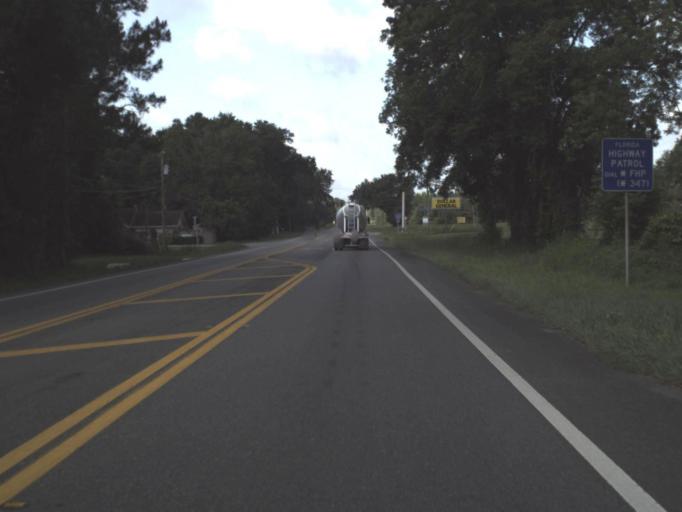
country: US
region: Florida
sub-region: Columbia County
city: Lake City
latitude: 30.1502
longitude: -82.6960
